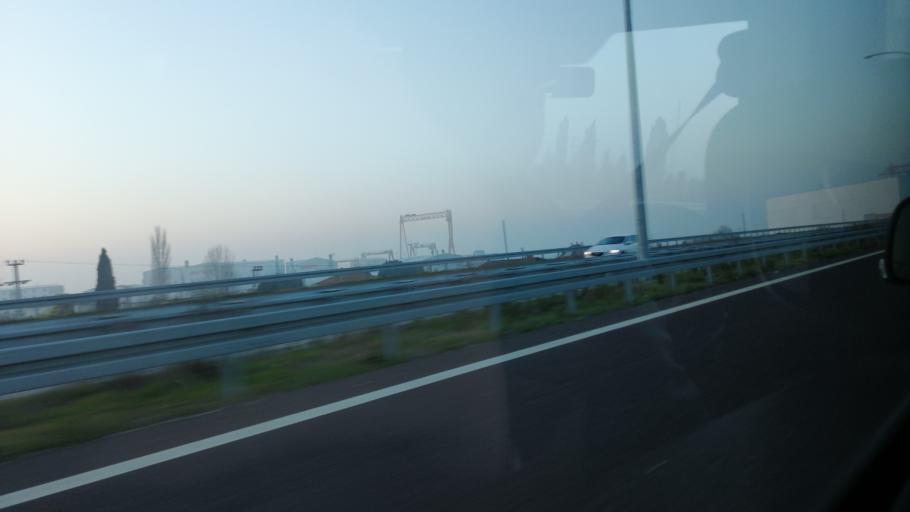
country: TR
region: Yalova
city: Altinova
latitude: 40.7229
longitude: 29.5030
